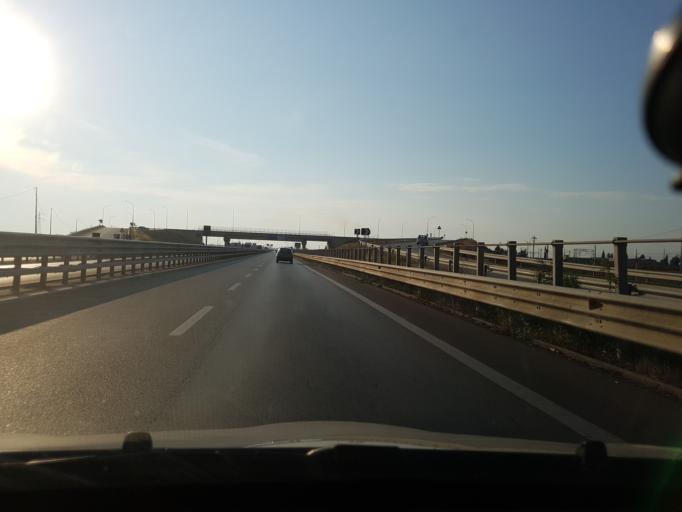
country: IT
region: Apulia
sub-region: Provincia di Foggia
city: Orta Nova
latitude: 41.3439
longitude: 15.7401
